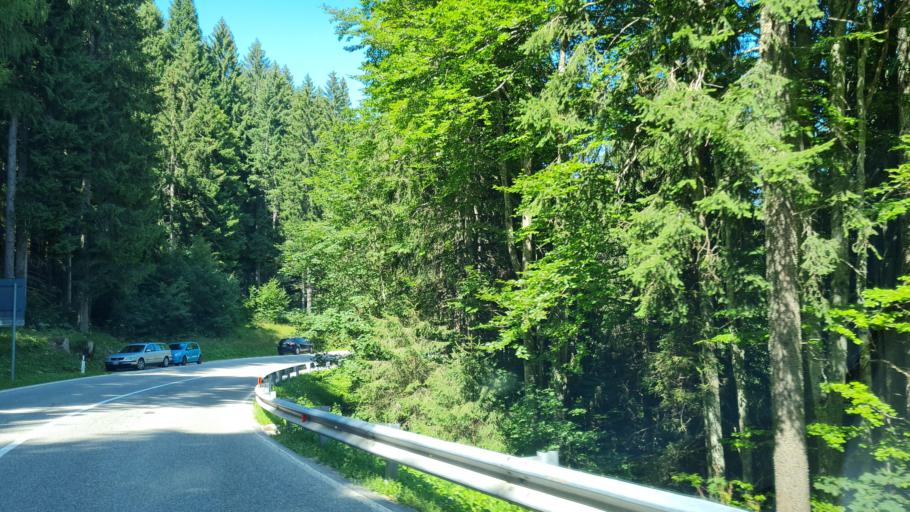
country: IT
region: Trentino-Alto Adige
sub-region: Provincia di Trento
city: Folgaria
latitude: 45.9214
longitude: 11.2074
